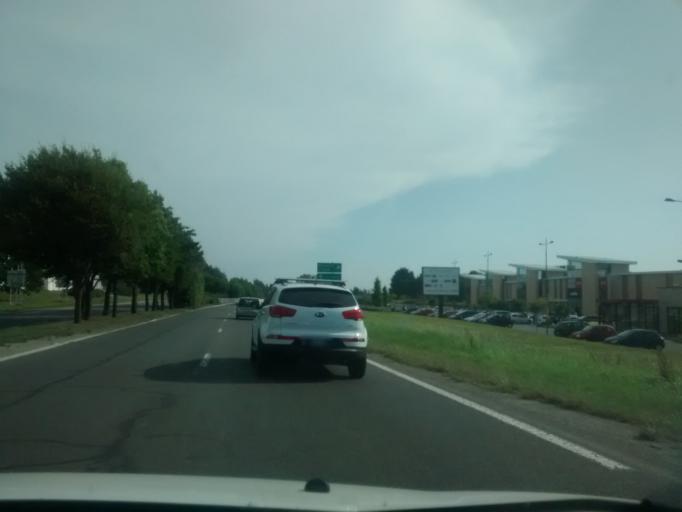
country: FR
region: Brittany
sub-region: Departement d'Ille-et-Vilaine
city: Saint-Jouan-des-Guerets
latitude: 48.6241
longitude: -1.9889
